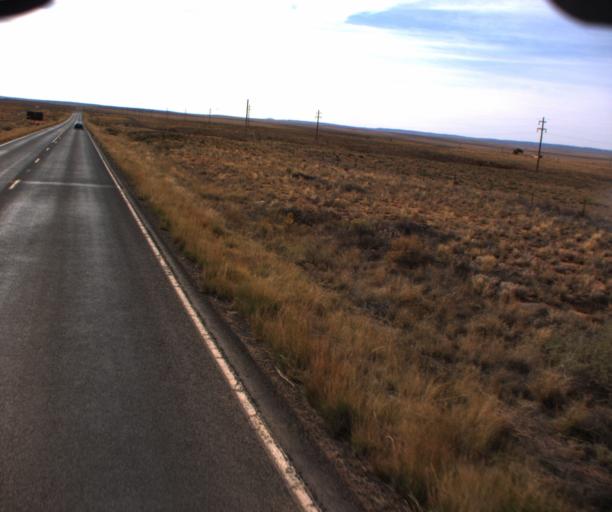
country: US
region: Arizona
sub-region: Apache County
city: Chinle
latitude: 35.9919
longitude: -109.6017
